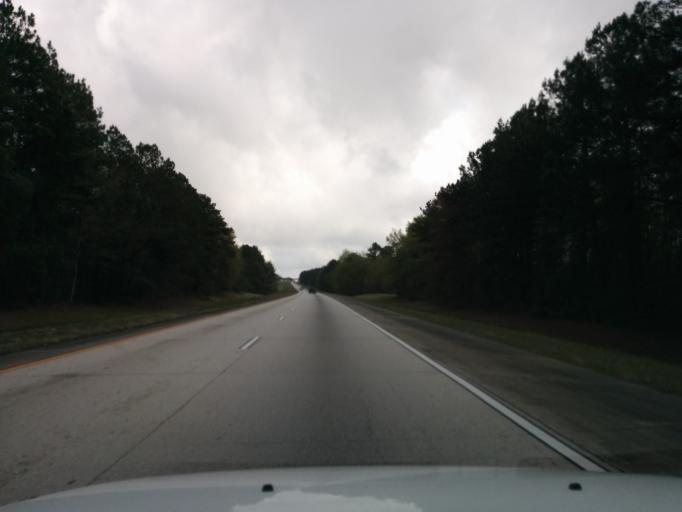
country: US
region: Georgia
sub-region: Candler County
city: Metter
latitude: 32.3261
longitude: -81.9292
